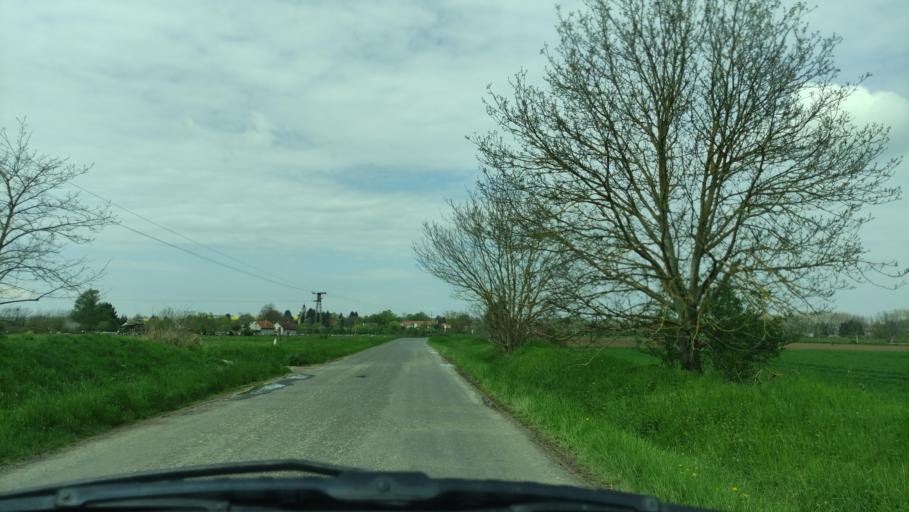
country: HU
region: Baranya
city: Sasd
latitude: 46.3057
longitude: 18.1469
